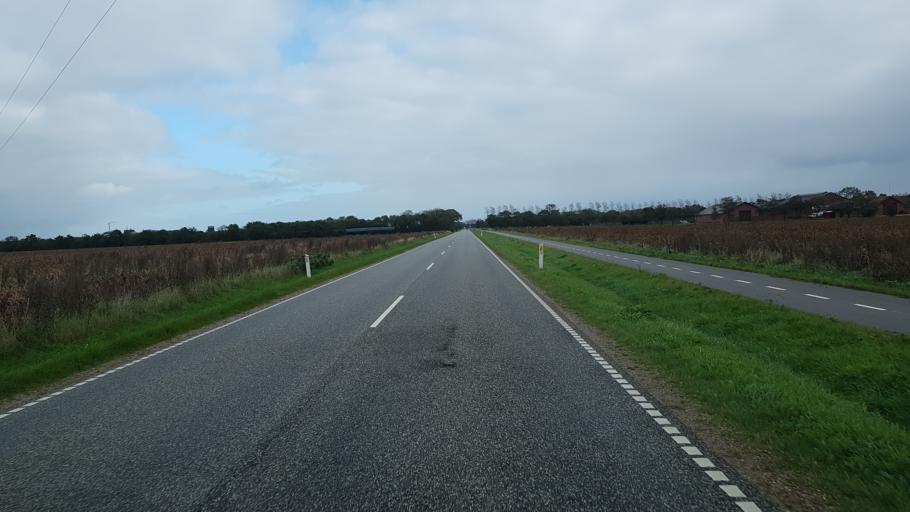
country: DK
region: South Denmark
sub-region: Billund Kommune
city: Grindsted
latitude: 55.7642
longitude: 8.8482
